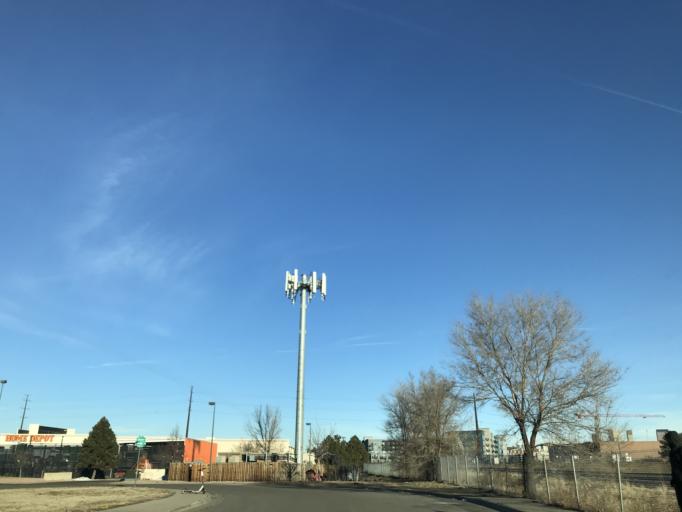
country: US
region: Colorado
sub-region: Denver County
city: Denver
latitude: 39.7053
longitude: -104.9920
